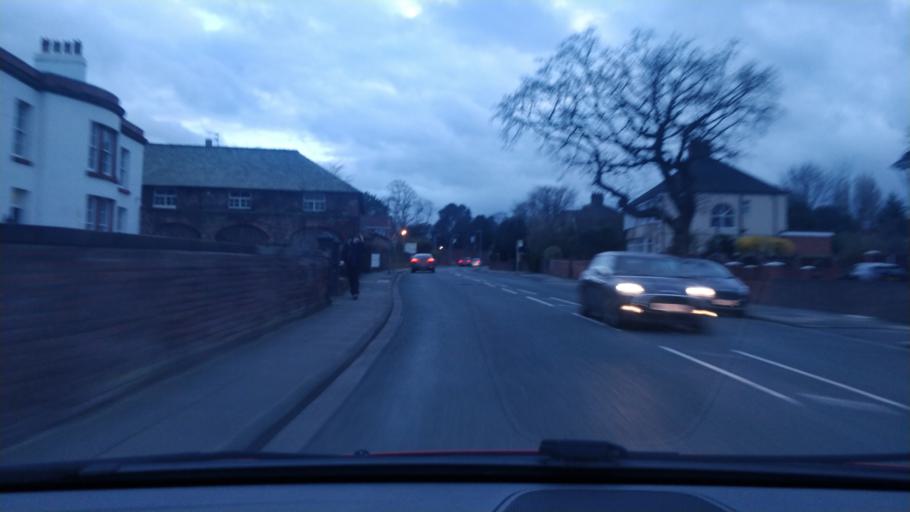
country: GB
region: England
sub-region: Knowsley
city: Knowsley
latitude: 53.4273
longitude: -2.8860
